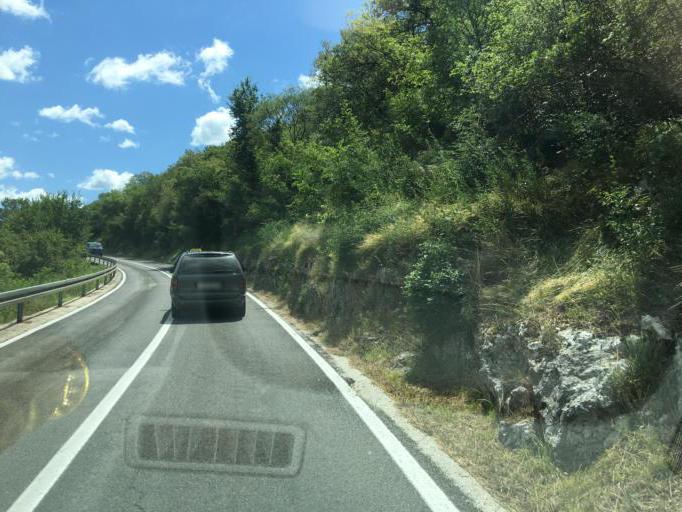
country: HR
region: Istarska
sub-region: Grad Rovinj
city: Rovinj
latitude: 45.1251
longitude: 13.7507
